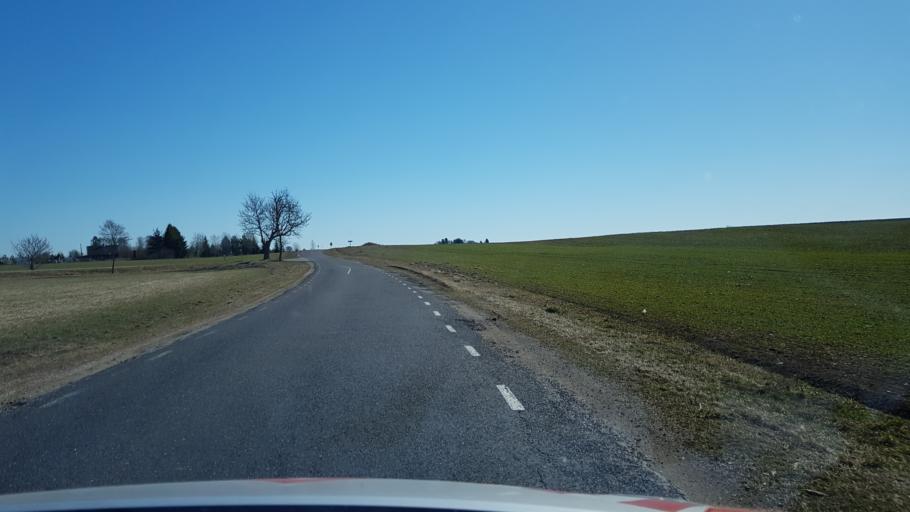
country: EE
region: Laeaene-Virumaa
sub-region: Haljala vald
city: Haljala
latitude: 59.4354
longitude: 26.2017
